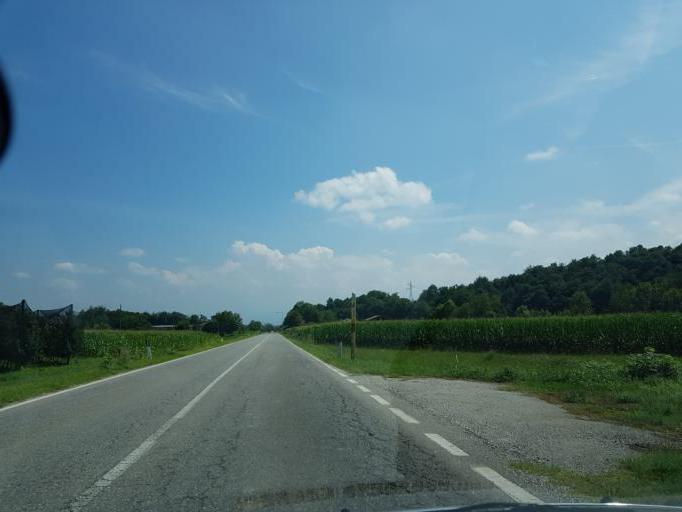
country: IT
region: Piedmont
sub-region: Provincia di Cuneo
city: Montemale di Cuneo
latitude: 44.4454
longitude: 7.4025
